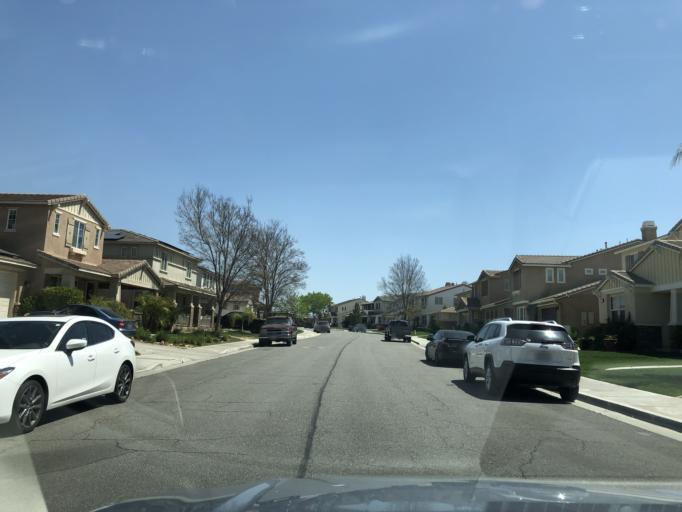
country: US
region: California
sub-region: Riverside County
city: Calimesa
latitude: 33.9619
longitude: -117.0518
